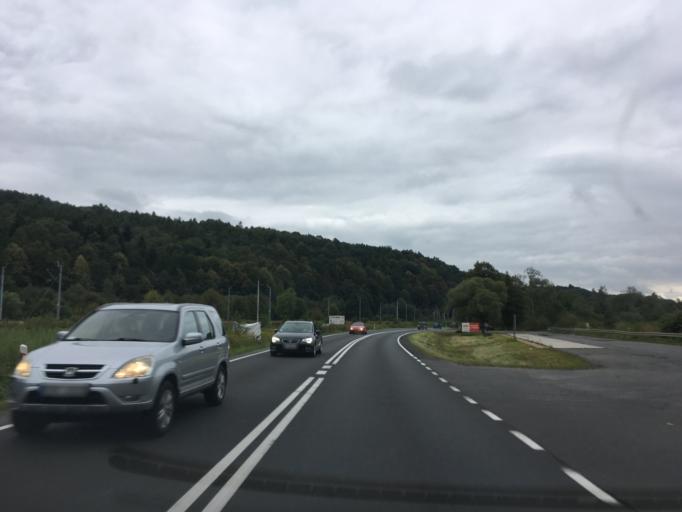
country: PL
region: Lesser Poland Voivodeship
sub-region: Powiat suski
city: Zembrzyce
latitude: 49.7618
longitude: 19.5987
